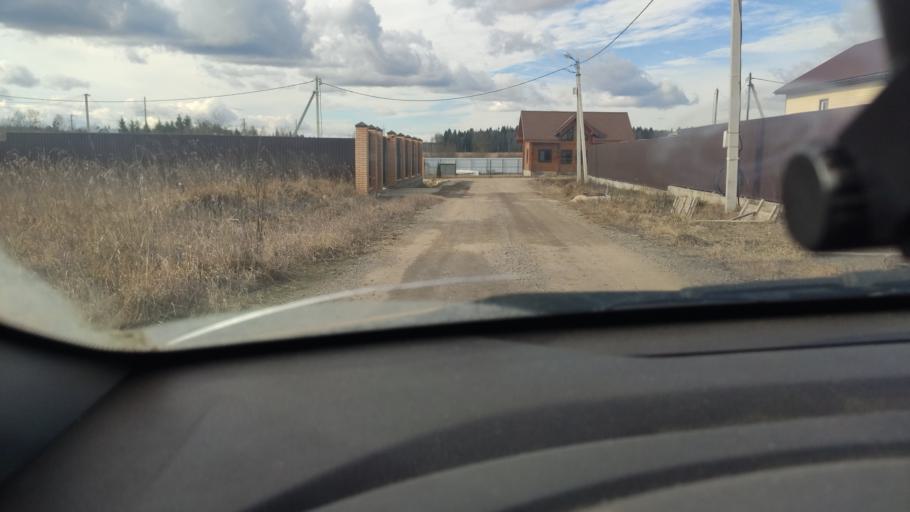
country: RU
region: Moskovskaya
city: Ruza
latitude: 55.7633
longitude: 36.1292
